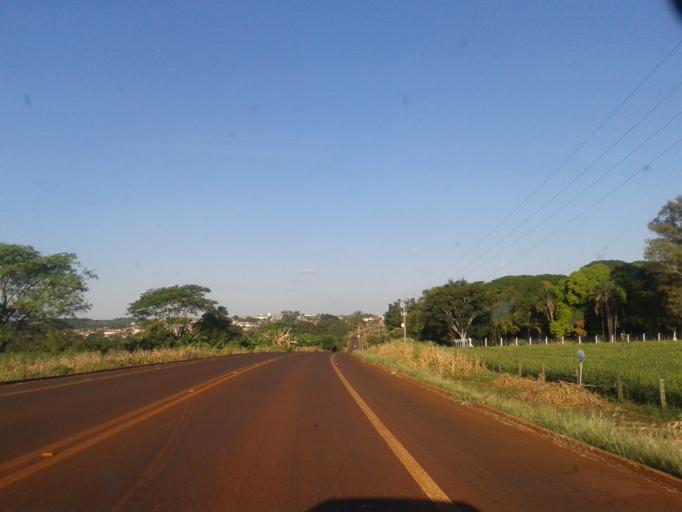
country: BR
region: Minas Gerais
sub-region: Capinopolis
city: Capinopolis
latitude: -18.6836
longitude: -49.5925
